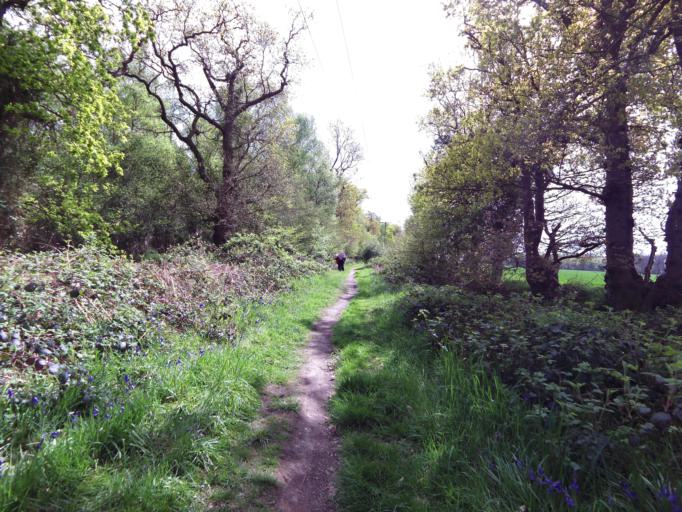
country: GB
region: England
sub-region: Suffolk
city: Ipswich
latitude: 52.0046
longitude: 1.1407
